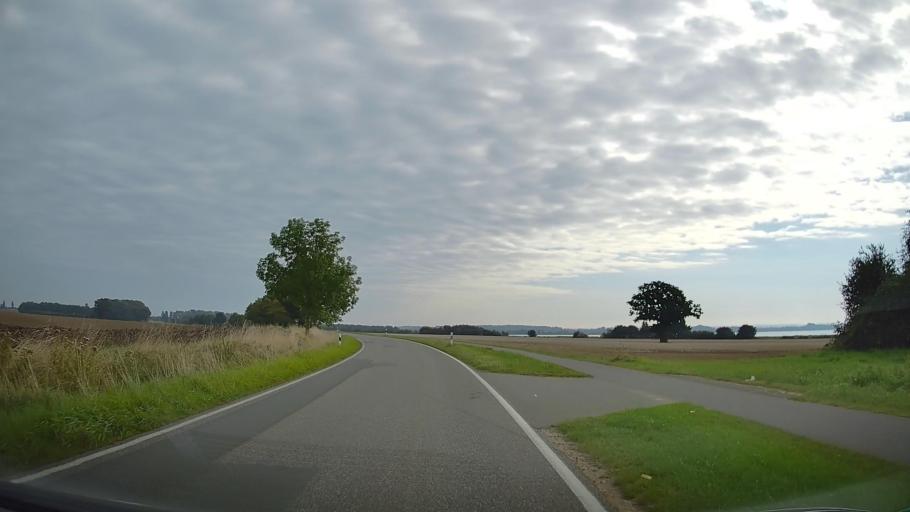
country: DE
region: Schleswig-Holstein
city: Panker
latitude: 54.3395
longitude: 10.6206
